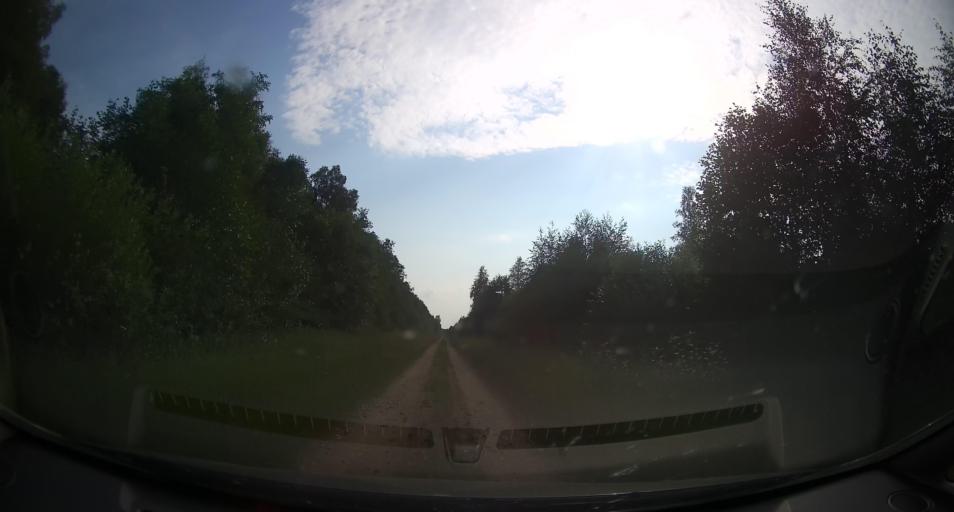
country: EE
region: Laeaene
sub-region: Lihula vald
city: Lihula
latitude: 58.6359
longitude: 23.7536
